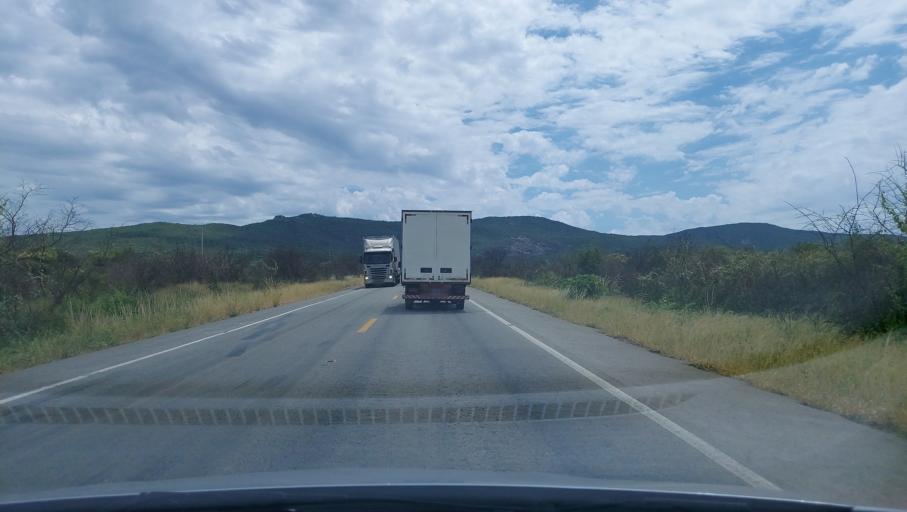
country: BR
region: Bahia
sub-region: Seabra
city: Seabra
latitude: -12.4551
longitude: -42.1902
